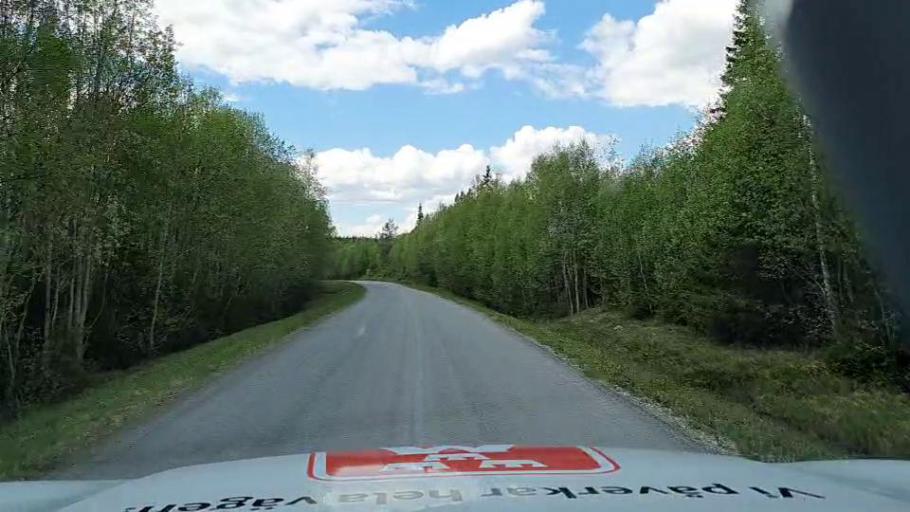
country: NO
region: Nord-Trondelag
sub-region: Lierne
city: Sandvika
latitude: 64.1340
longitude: 14.1083
